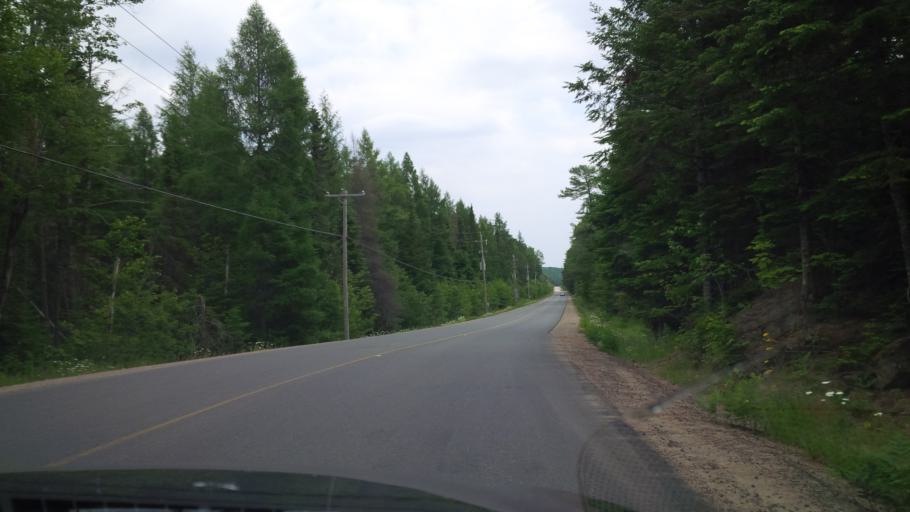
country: CA
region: Ontario
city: Huntsville
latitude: 45.5950
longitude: -79.2062
